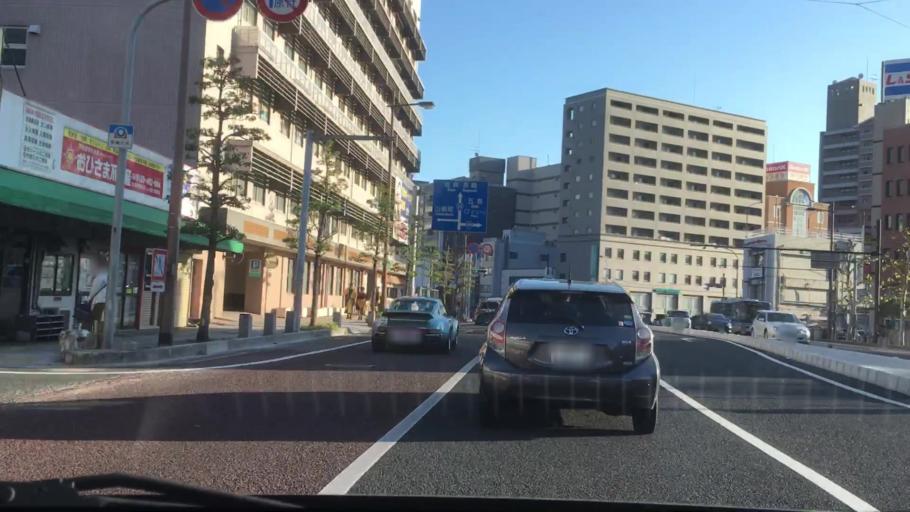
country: JP
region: Nagasaki
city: Sasebo
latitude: 33.1686
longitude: 129.7242
